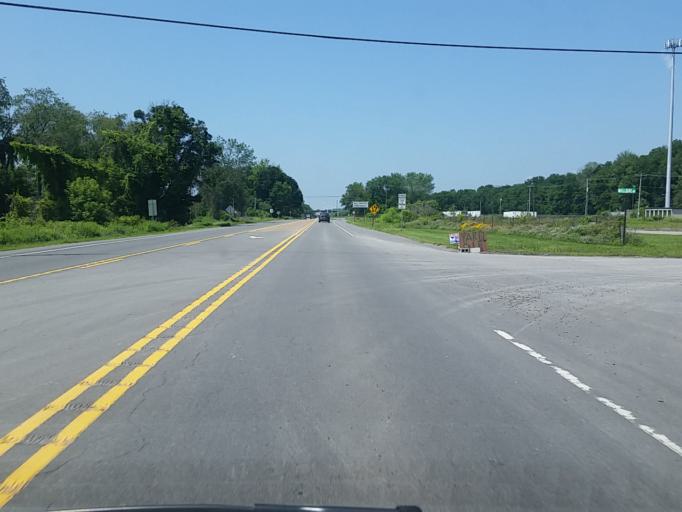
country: US
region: Pennsylvania
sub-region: Columbia County
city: Mifflinville
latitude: 41.0362
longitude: -76.3253
